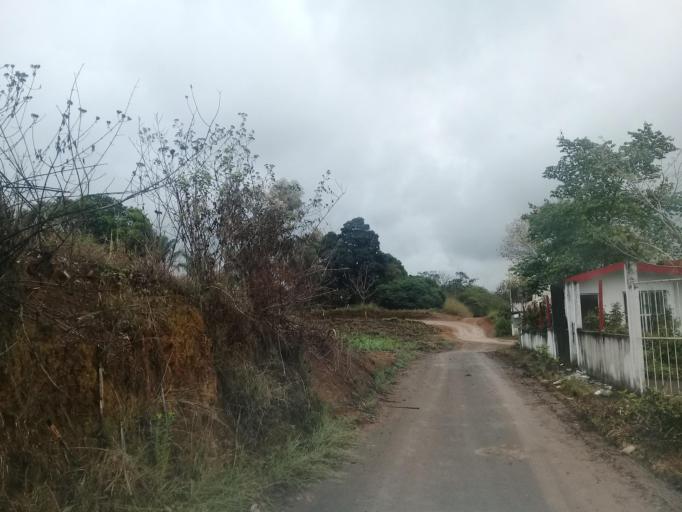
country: MX
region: Veracruz
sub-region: Cordoba
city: San Jose de Tapia
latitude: 18.8411
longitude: -96.9541
